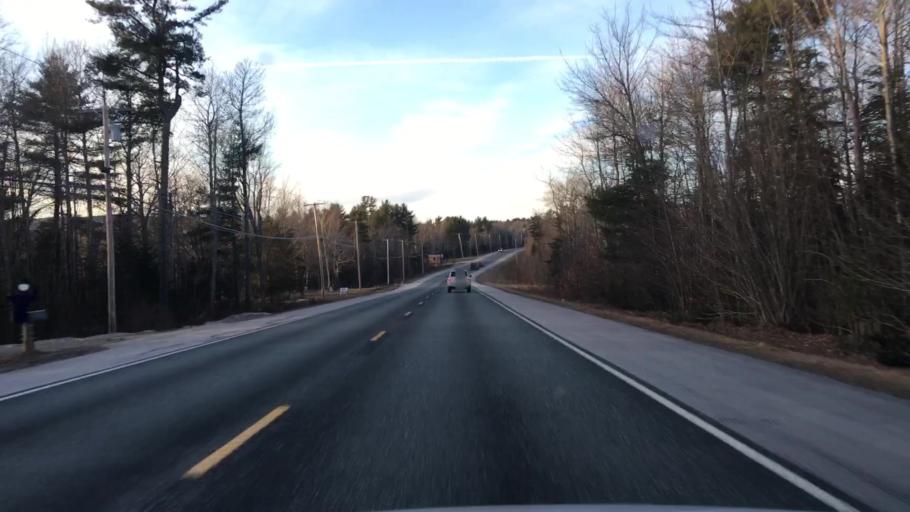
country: US
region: Maine
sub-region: Hancock County
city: Dedham
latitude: 44.6319
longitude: -68.5426
